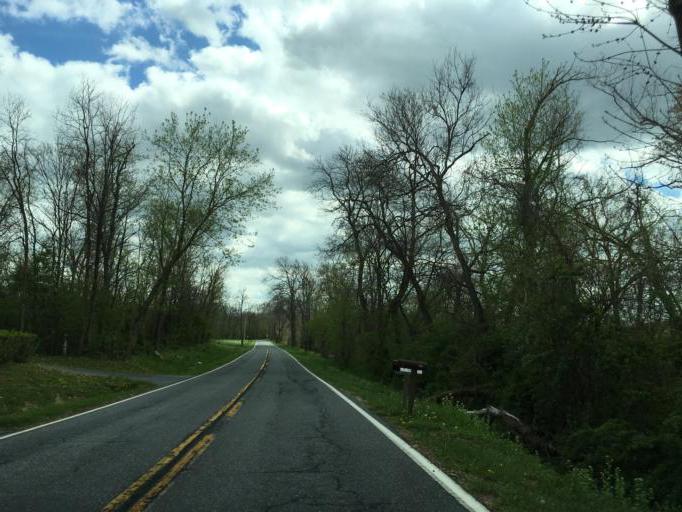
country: US
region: Maryland
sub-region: Frederick County
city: Thurmont
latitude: 39.5731
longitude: -77.3917
